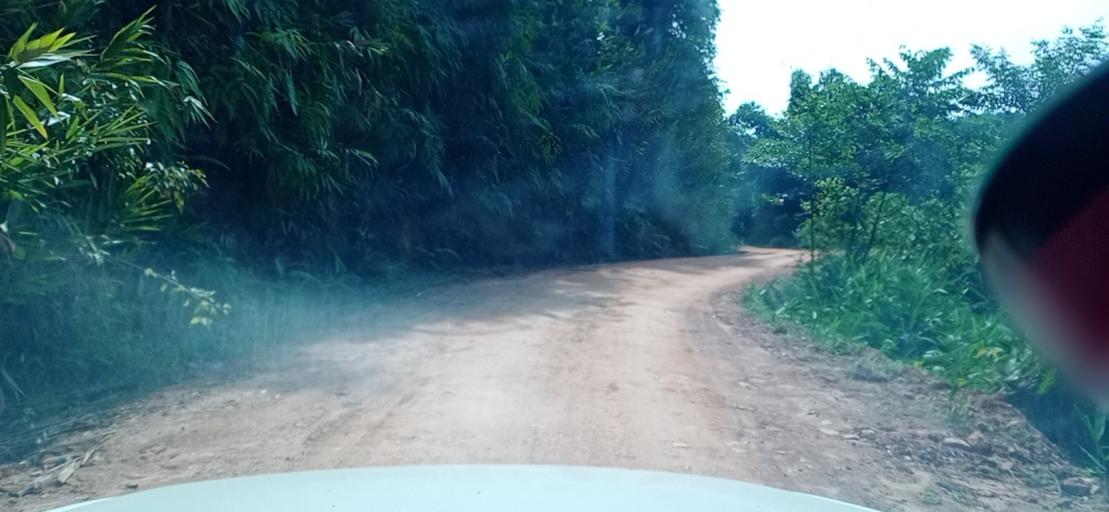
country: TH
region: Changwat Bueng Kan
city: Pak Khat
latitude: 18.6367
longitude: 103.2589
